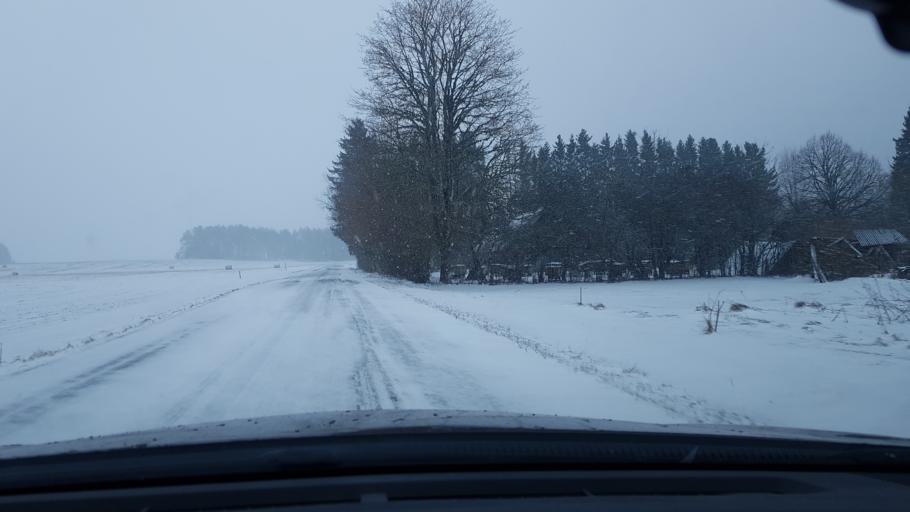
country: EE
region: Harju
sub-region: Anija vald
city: Kehra
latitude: 59.1996
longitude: 25.4023
